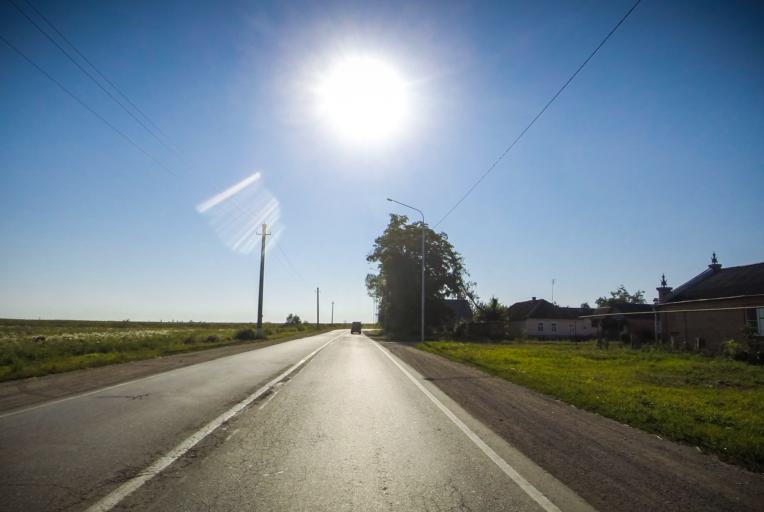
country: RU
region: North Ossetia
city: Arkhonskaya
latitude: 43.1190
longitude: 44.5223
